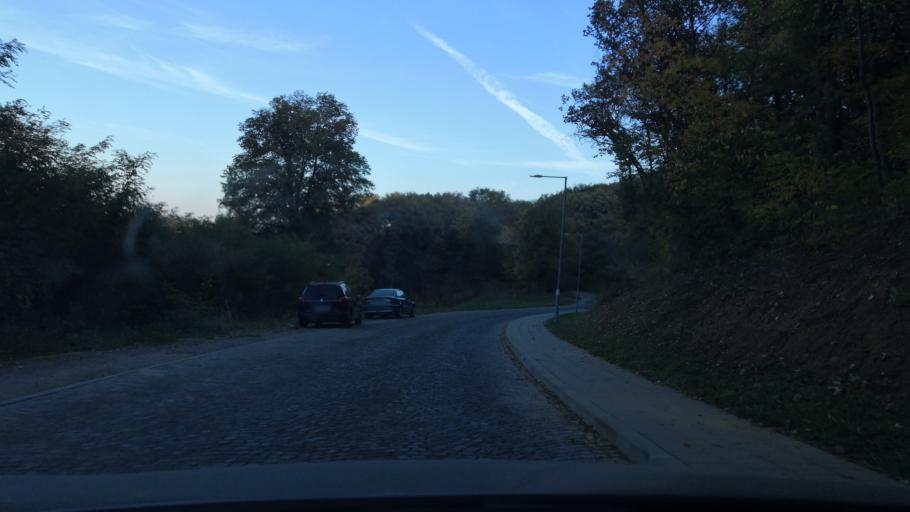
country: RS
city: Vrdnik
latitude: 45.1464
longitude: 19.7768
